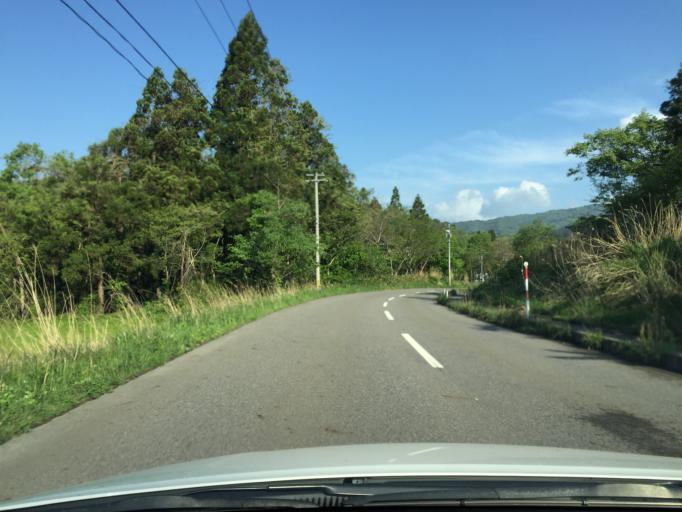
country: JP
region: Fukushima
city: Kitakata
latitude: 37.6544
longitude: 139.7609
